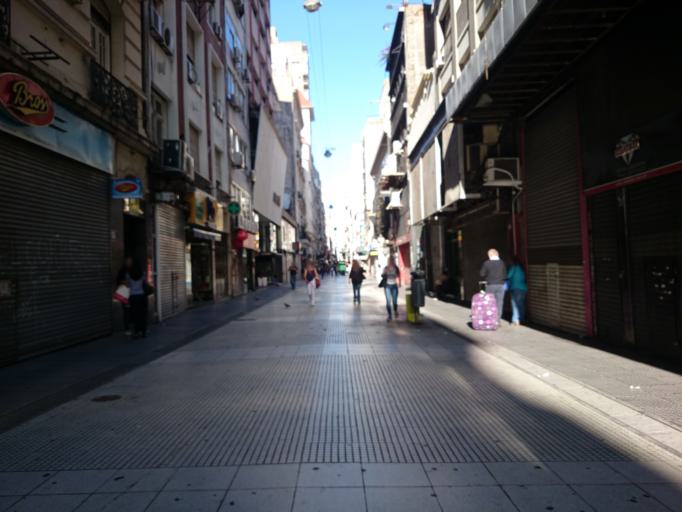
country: AR
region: Buenos Aires F.D.
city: Buenos Aires
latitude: -34.6023
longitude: -58.3756
